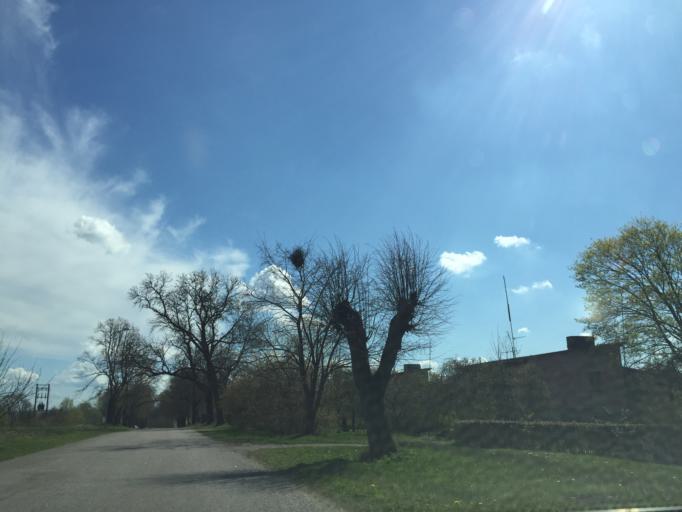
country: LV
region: Strenci
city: Strenci
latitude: 57.5477
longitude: 25.7110
